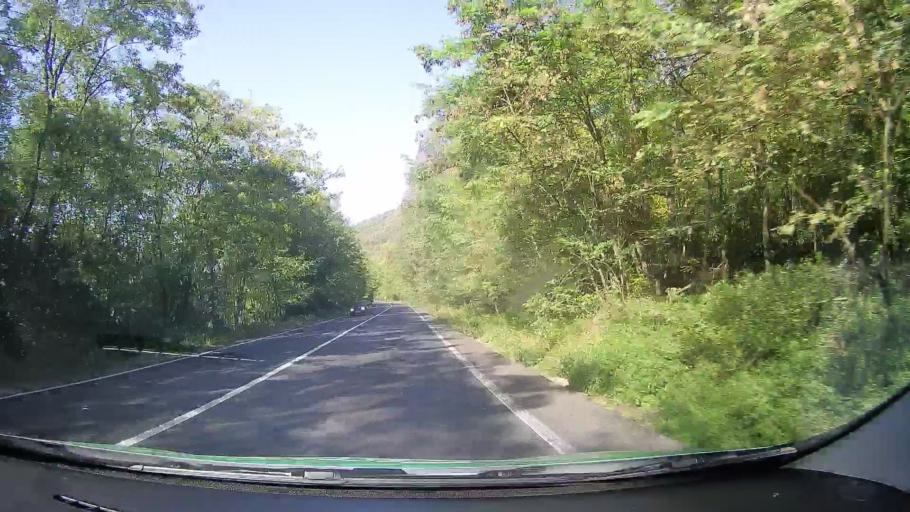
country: RO
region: Arad
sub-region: Comuna Savarsin
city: Savarsin
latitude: 46.0098
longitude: 22.2710
